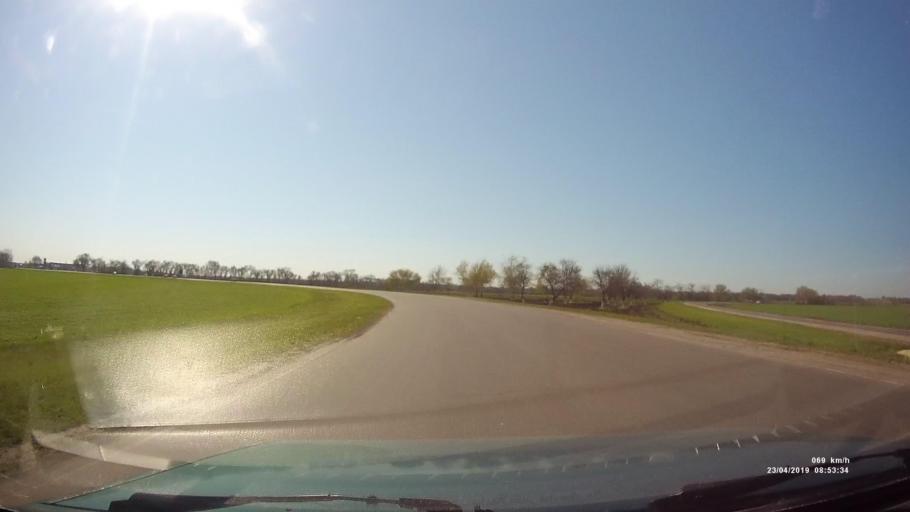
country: RU
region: Rostov
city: Sal'sk
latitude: 46.4742
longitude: 41.4754
